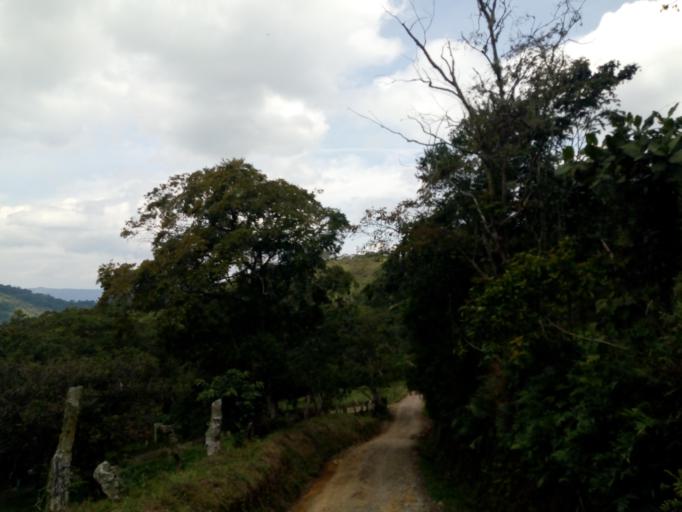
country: CO
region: Boyaca
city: Moniquira
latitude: 5.8655
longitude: -73.5190
